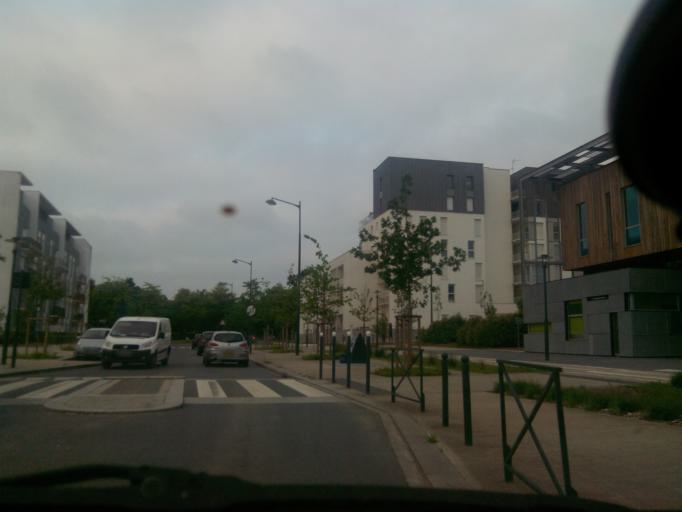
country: FR
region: Brittany
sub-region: Departement d'Ille-et-Vilaine
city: Saint-Gregoire
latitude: 48.1302
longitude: -1.6956
